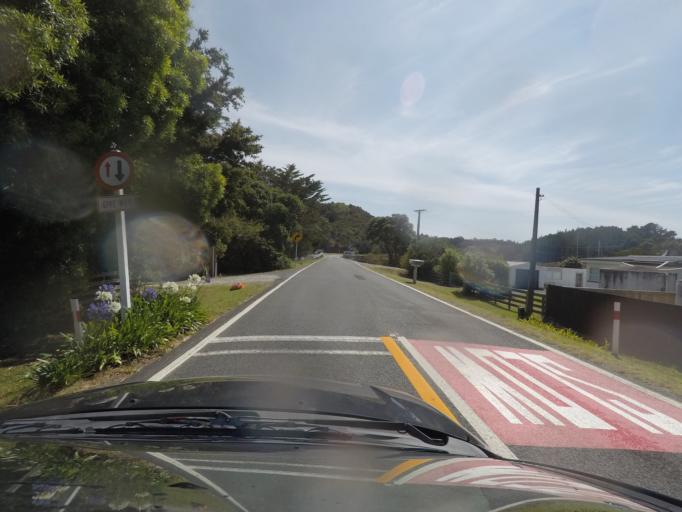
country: NZ
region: Auckland
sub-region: Auckland
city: Warkworth
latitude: -36.3090
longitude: 174.7775
